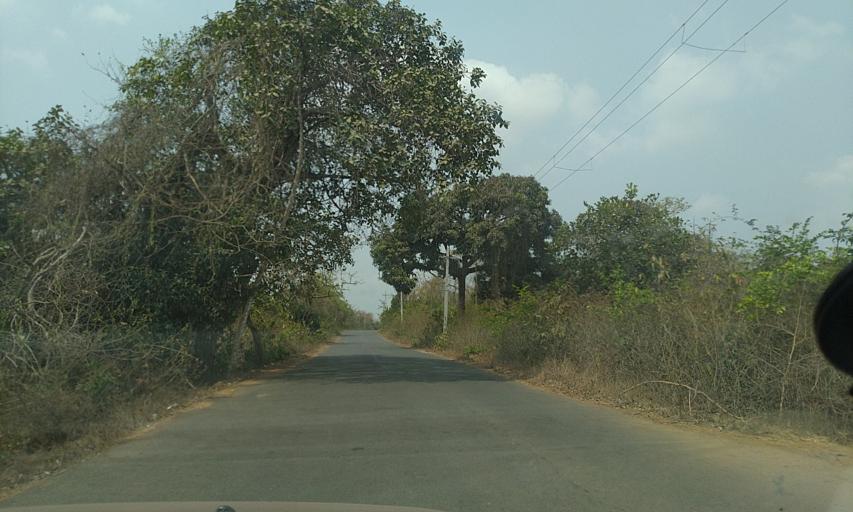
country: IN
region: Goa
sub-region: North Goa
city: Goa Velha
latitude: 15.4828
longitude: 73.8970
